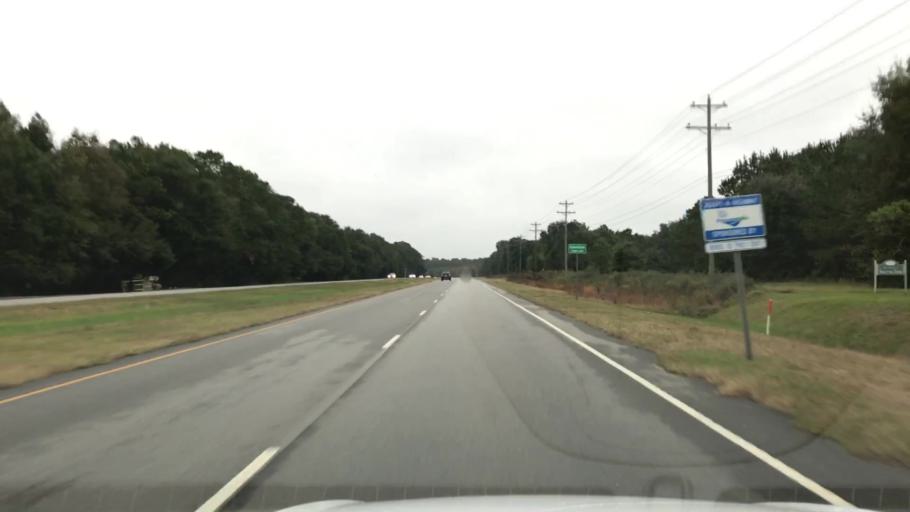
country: US
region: South Carolina
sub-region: Charleston County
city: Isle of Palms
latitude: 32.9129
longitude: -79.7208
